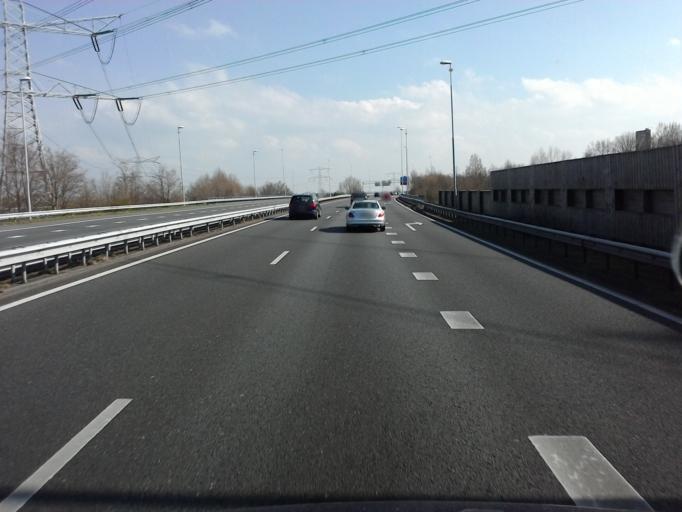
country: NL
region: North Holland
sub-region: Gemeente Zaanstad
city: Zaandam
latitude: 52.4589
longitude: 4.8363
